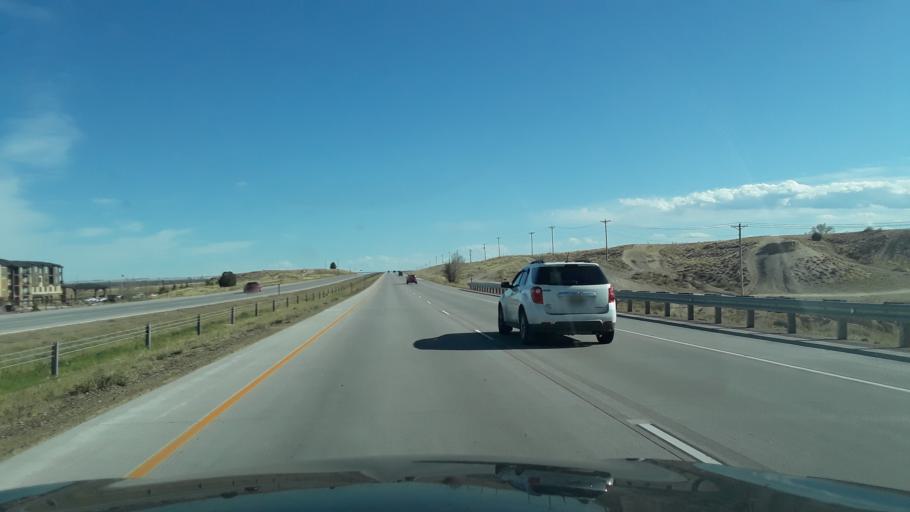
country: US
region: Colorado
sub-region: Pueblo County
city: Pueblo
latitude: 38.3040
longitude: -104.6637
